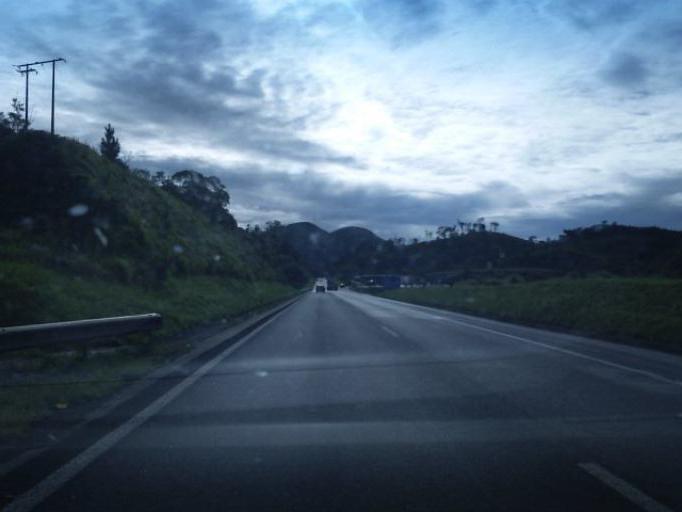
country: BR
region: Parana
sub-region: Antonina
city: Antonina
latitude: -25.1075
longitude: -48.7905
